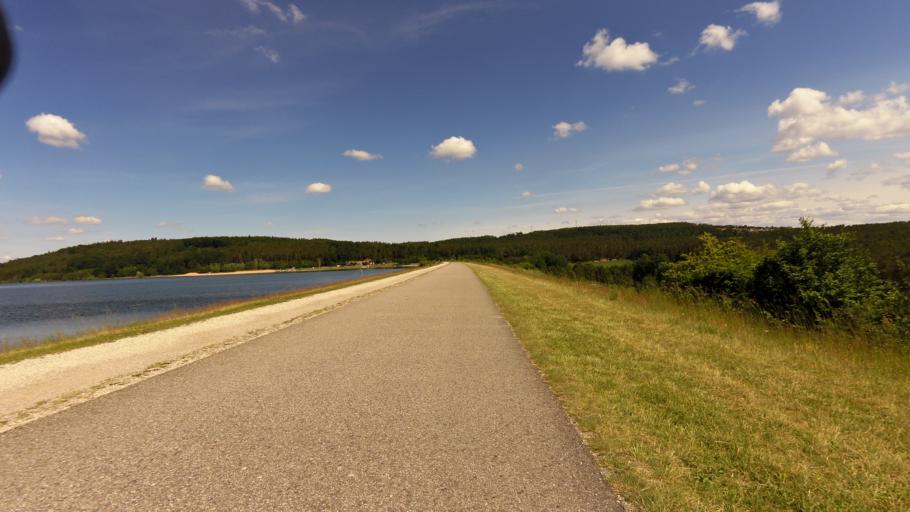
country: DE
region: Bavaria
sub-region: Regierungsbezirk Mittelfranken
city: Pleinfeld
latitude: 49.1276
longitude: 10.9636
